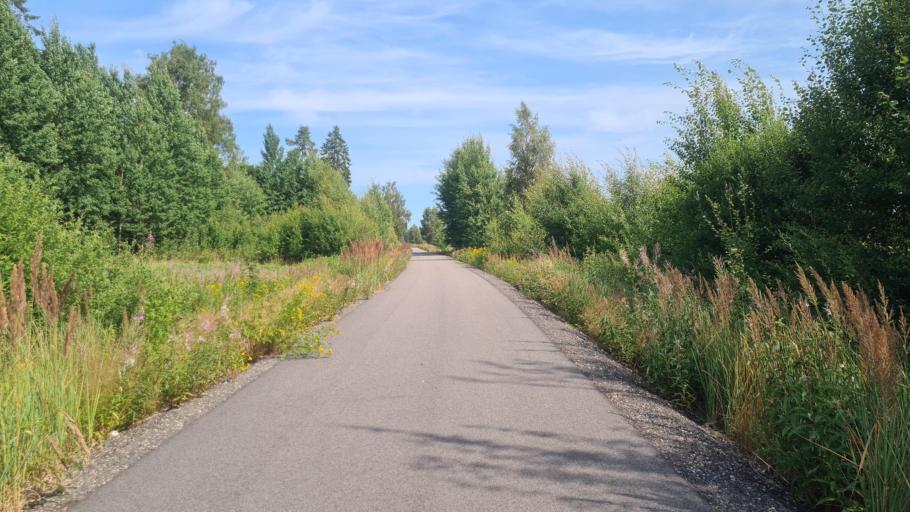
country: SE
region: Kronoberg
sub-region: Ljungby Kommun
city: Lagan
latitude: 56.8980
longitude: 13.9885
